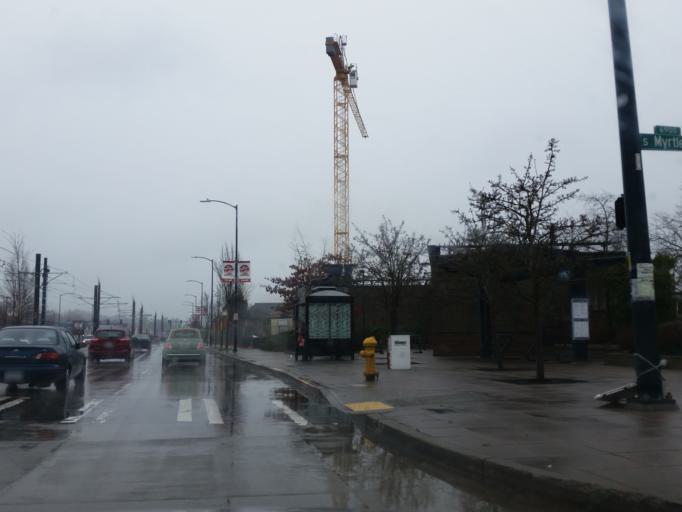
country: US
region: Washington
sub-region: King County
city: Riverton
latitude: 47.5389
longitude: -122.2818
